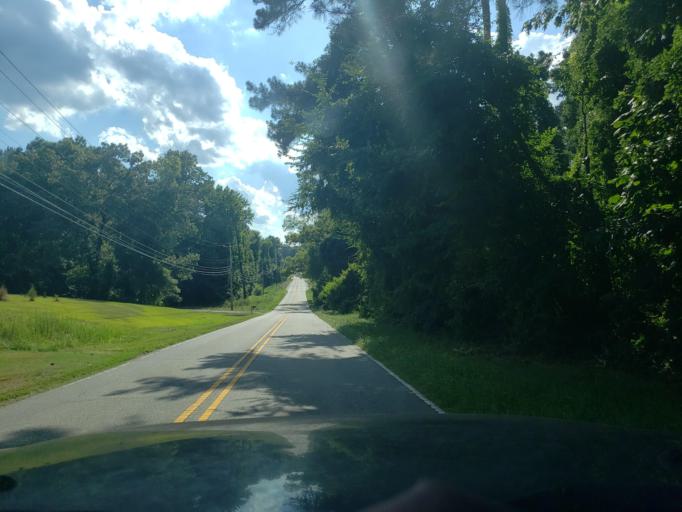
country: US
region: North Carolina
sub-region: Durham County
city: Durham
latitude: 35.9753
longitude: -78.9815
